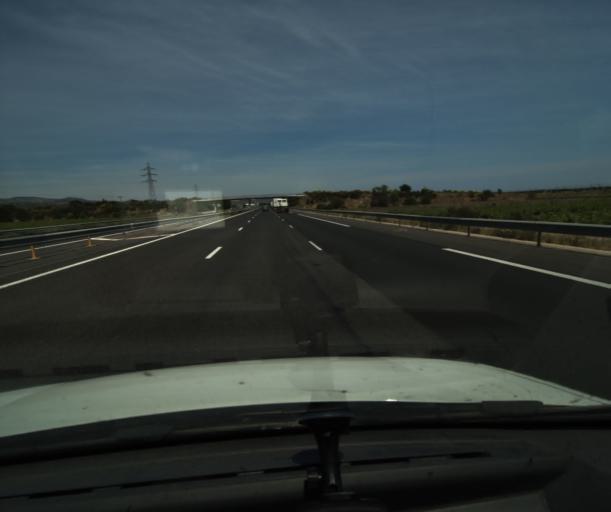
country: FR
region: Languedoc-Roussillon
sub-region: Departement des Pyrenees-Orientales
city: Salses-le-Chateau
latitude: 42.8019
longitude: 2.8988
